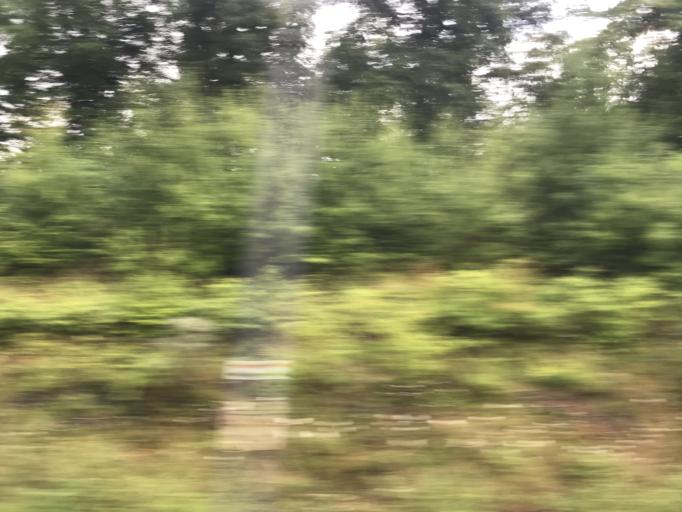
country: LU
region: Luxembourg
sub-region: Canton d'Esch-sur-Alzette
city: Leudelange
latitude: 49.5856
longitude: 6.0475
